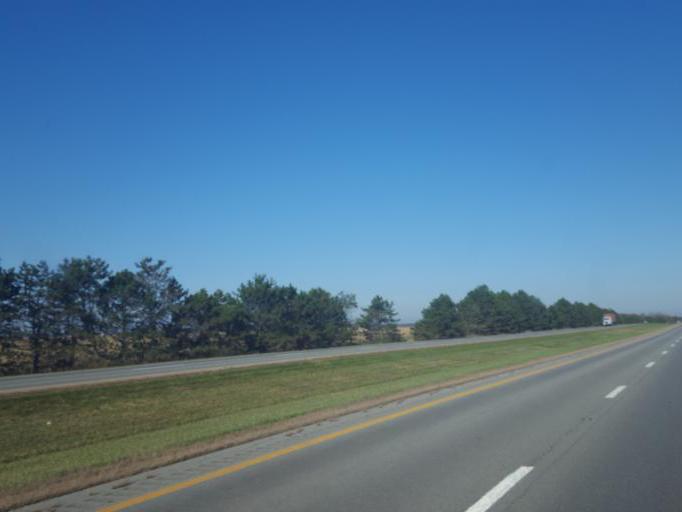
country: US
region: Ohio
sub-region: Wyandot County
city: Upper Sandusky
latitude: 40.7545
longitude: -83.2318
